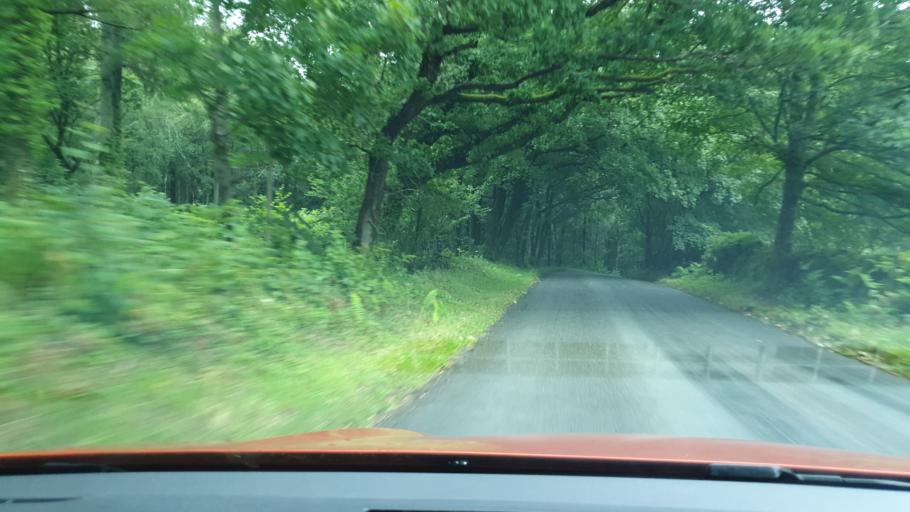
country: GB
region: England
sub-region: Cumbria
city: Seascale
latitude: 54.3949
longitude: -3.3430
